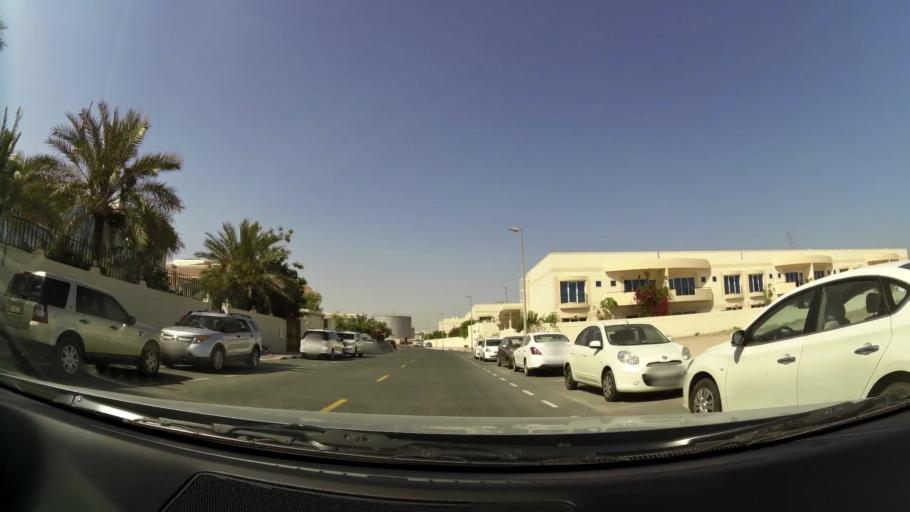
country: AE
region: Ash Shariqah
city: Sharjah
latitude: 25.2482
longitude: 55.2807
